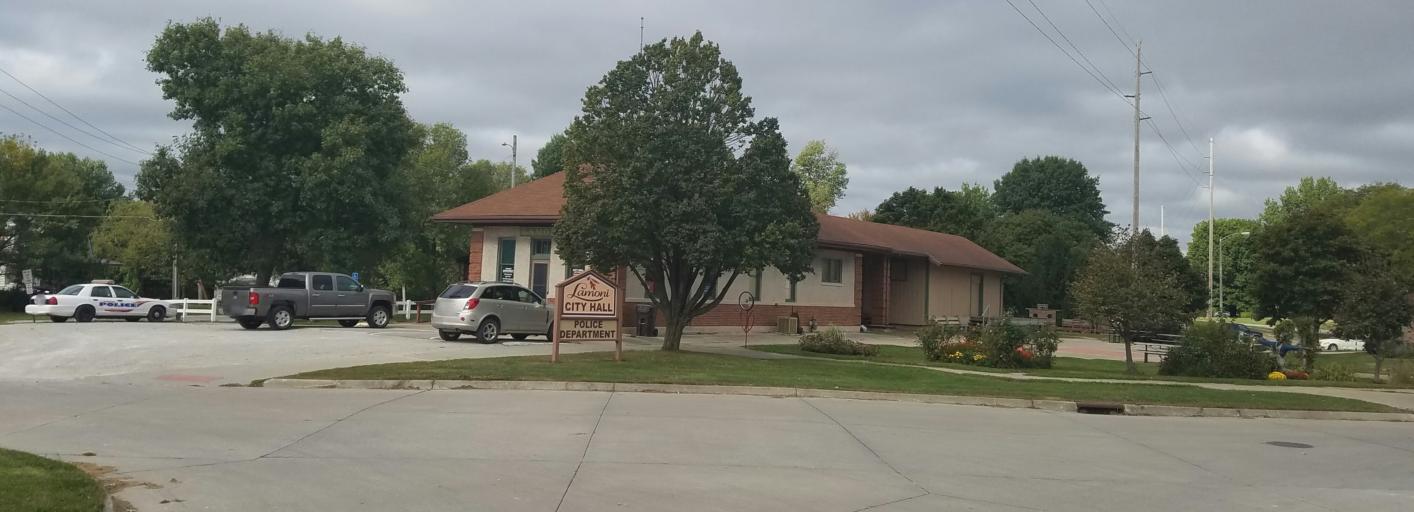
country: US
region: Iowa
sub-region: Decatur County
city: Lamoni
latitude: 40.6245
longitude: -93.9344
